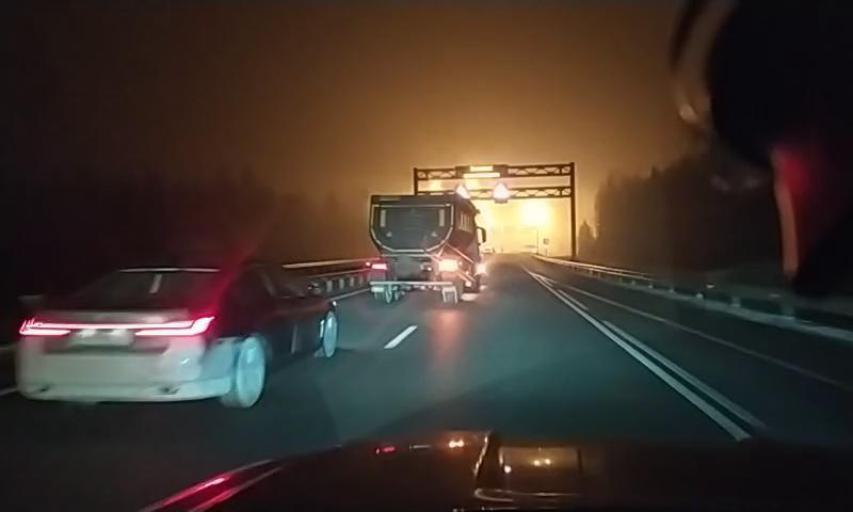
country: RU
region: Leningrad
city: Agalatovo
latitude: 60.2159
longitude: 30.3599
